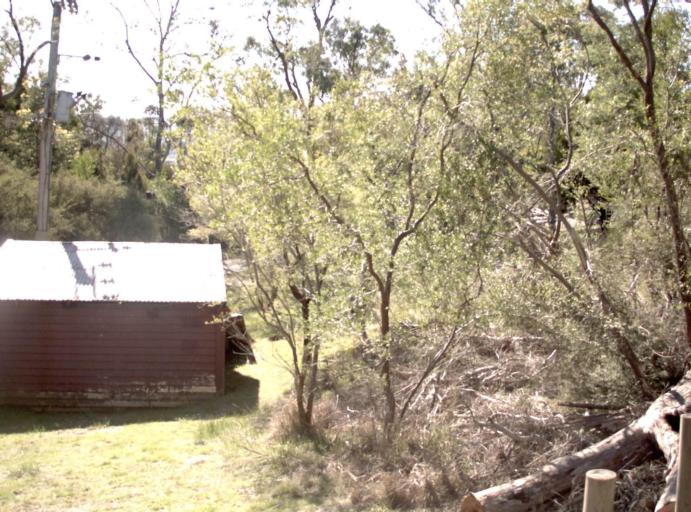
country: AU
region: Tasmania
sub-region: Launceston
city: Newstead
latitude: -41.4564
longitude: 147.1690
